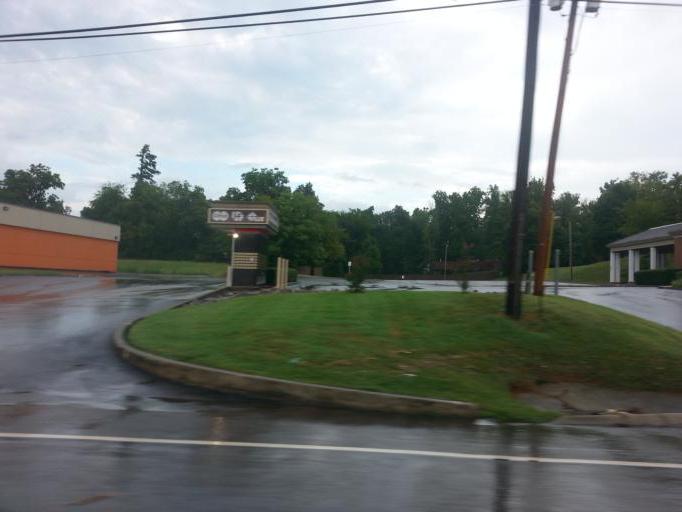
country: US
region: Tennessee
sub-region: Knox County
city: Knoxville
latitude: 35.9333
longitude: -83.9045
